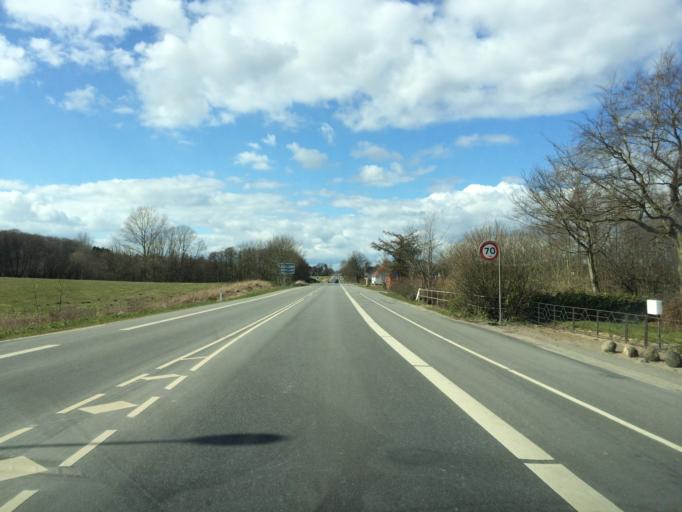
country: DK
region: South Denmark
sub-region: Assens Kommune
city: Arup
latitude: 55.4168
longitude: 10.0485
